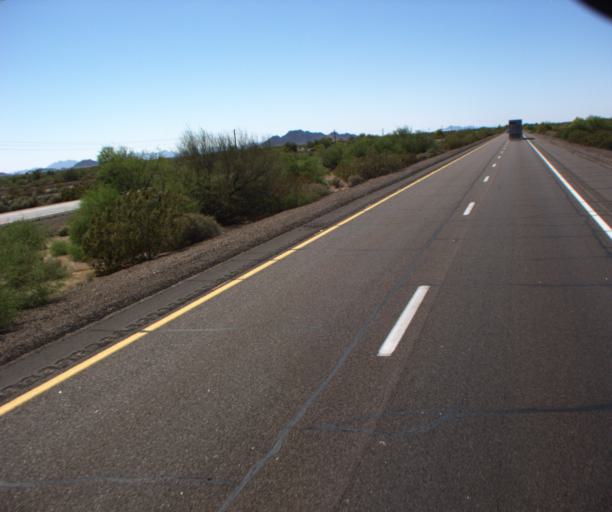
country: US
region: Arizona
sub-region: Maricopa County
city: Gila Bend
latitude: 32.8289
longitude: -113.4104
